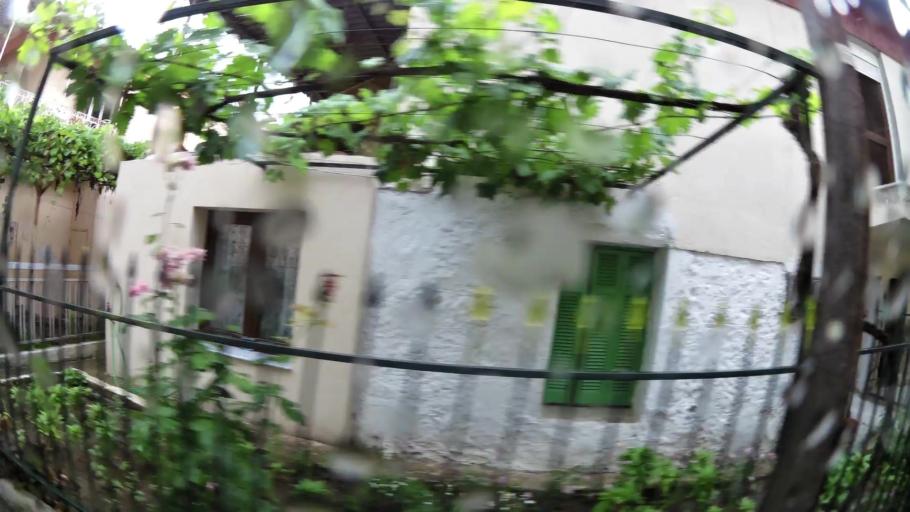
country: GR
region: Central Macedonia
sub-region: Nomos Imathias
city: Veroia
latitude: 40.5342
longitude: 22.2032
